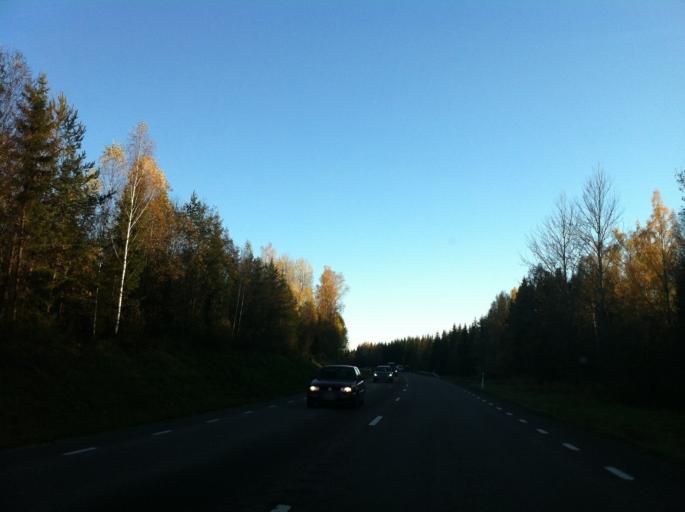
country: SE
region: Dalarna
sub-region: Faluns Kommun
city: Falun
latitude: 60.6546
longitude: 15.5559
